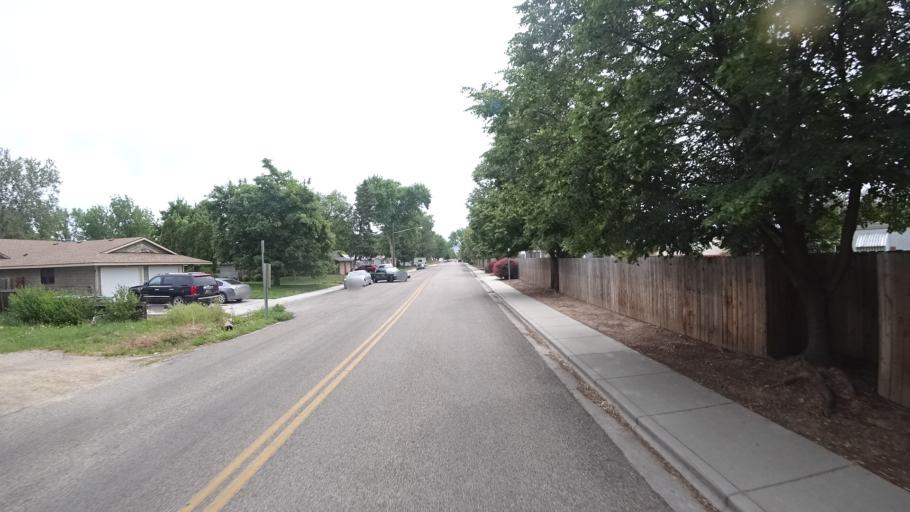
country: US
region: Idaho
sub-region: Ada County
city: Boise
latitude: 43.5771
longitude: -116.2108
